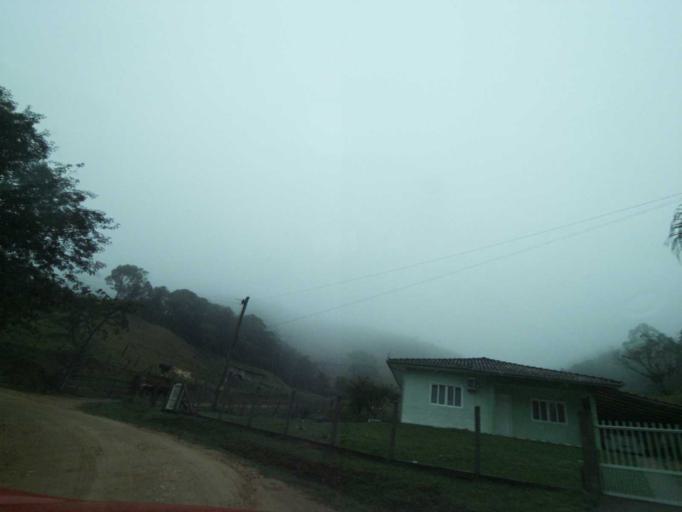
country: BR
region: Santa Catarina
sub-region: Anitapolis
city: Anitapolis
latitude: -27.9115
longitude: -49.1171
